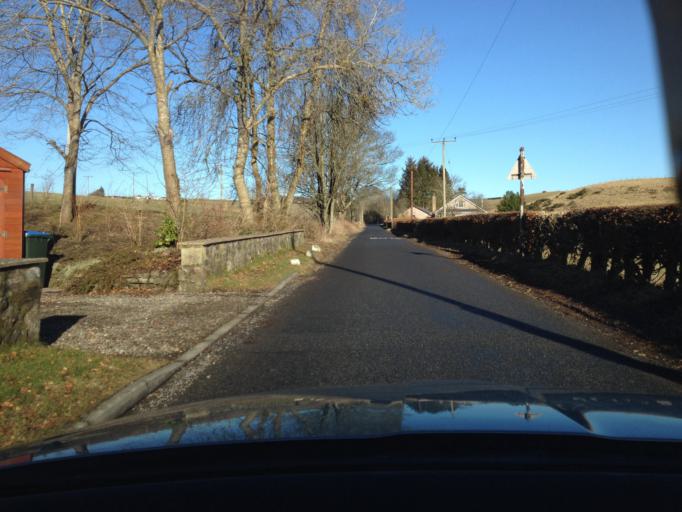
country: GB
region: Scotland
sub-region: Perth and Kinross
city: Bridge of Earn
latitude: 56.2904
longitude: -3.3964
